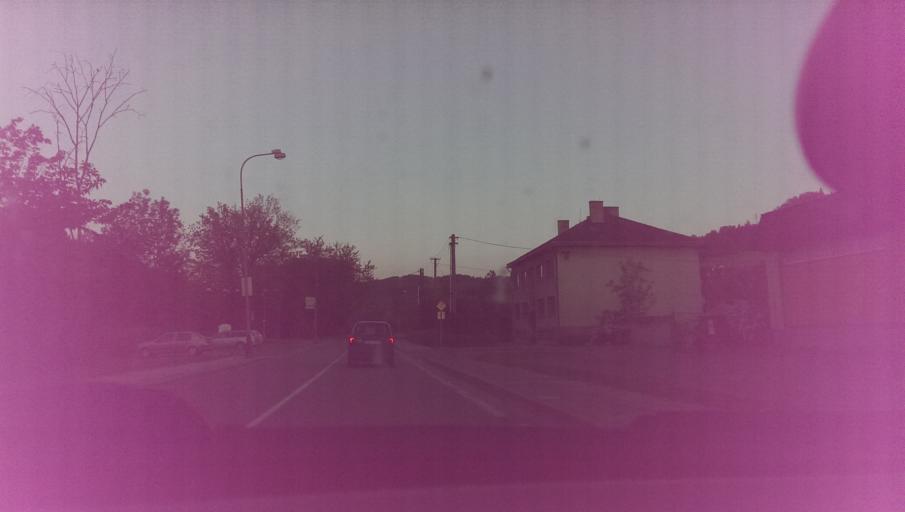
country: CZ
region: Zlin
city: Valasska Polanka
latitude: 49.2576
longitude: 17.9961
